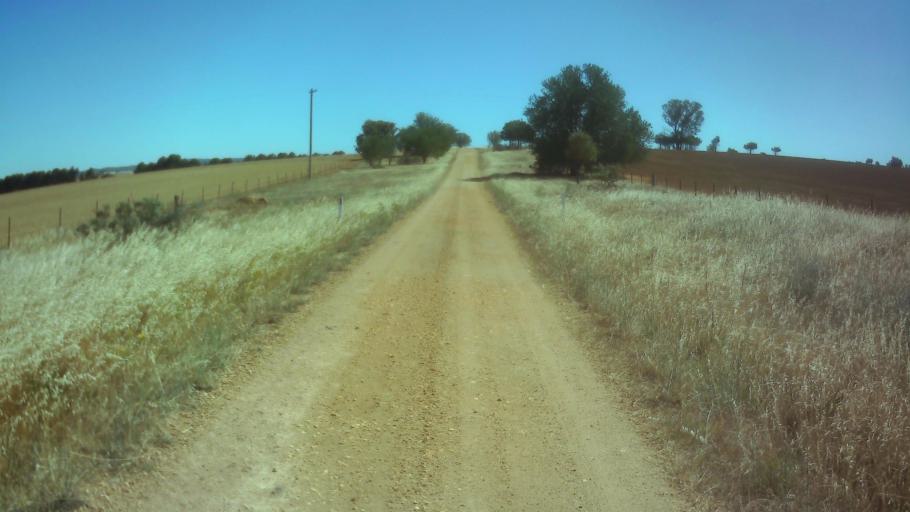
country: AU
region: New South Wales
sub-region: Weddin
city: Grenfell
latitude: -33.9671
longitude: 148.3444
